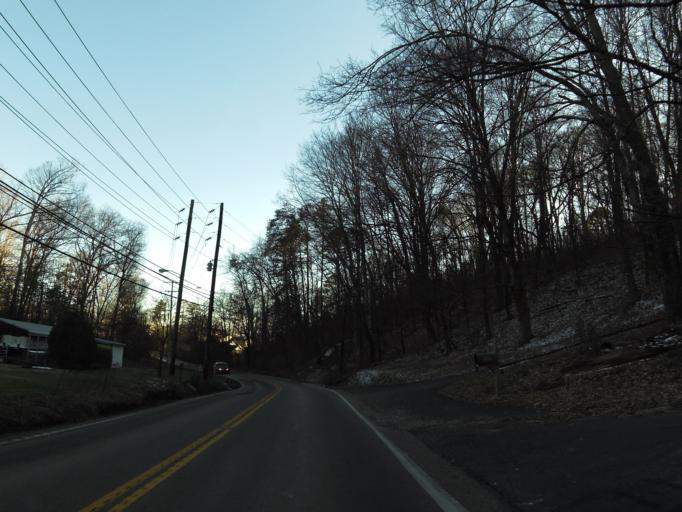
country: US
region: Tennessee
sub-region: Knox County
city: Farragut
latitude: 35.8818
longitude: -84.1288
